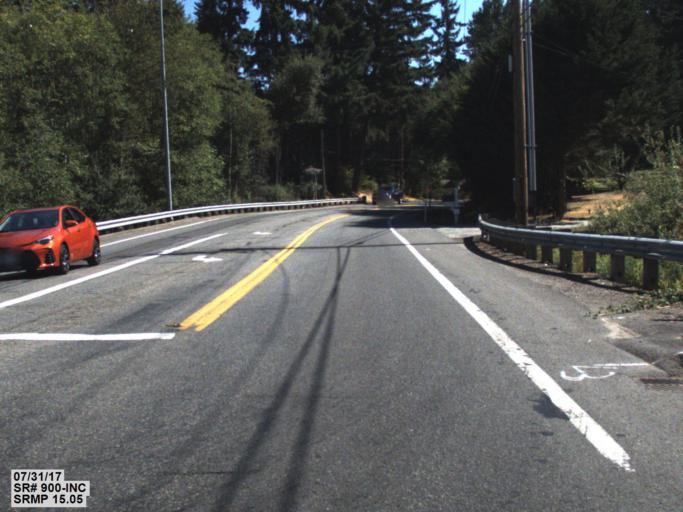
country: US
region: Washington
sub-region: King County
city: Newcastle
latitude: 47.5056
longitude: -122.1433
